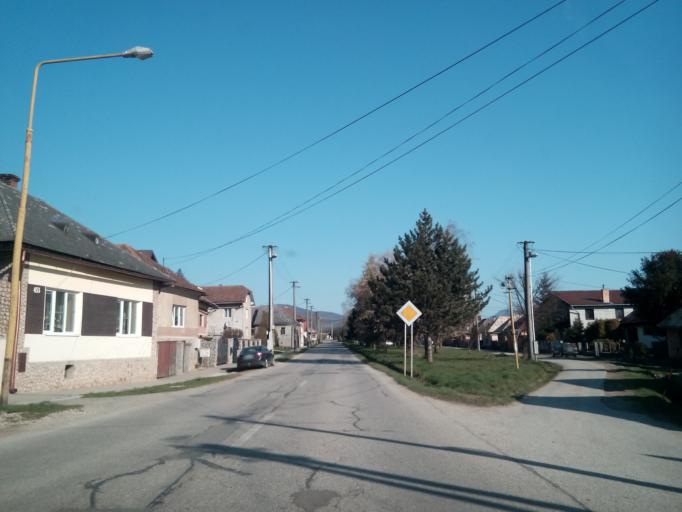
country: SK
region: Kosicky
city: Dobsina
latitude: 48.6609
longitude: 20.3630
